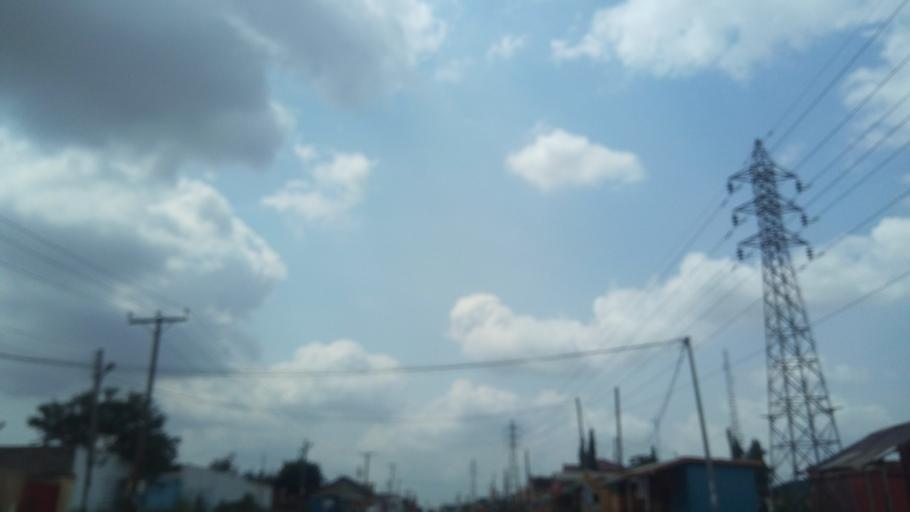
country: GH
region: Greater Accra
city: Tema
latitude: 5.7075
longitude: -0.0226
